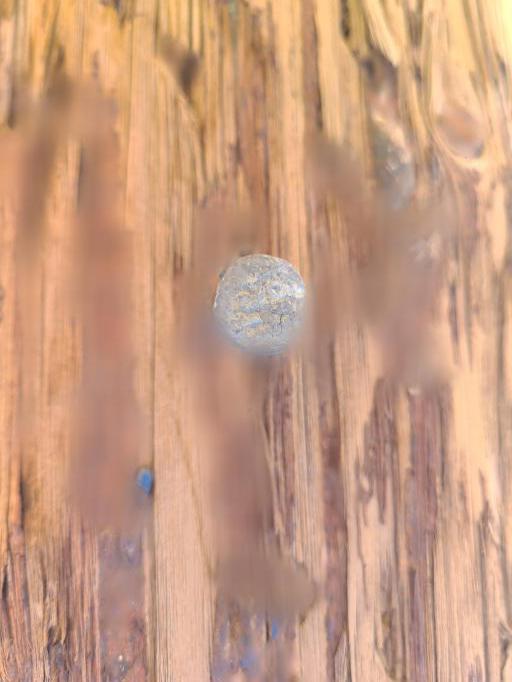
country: US
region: California
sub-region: San Bernardino County
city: Big Bear City
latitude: 34.3431
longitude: -116.8417
